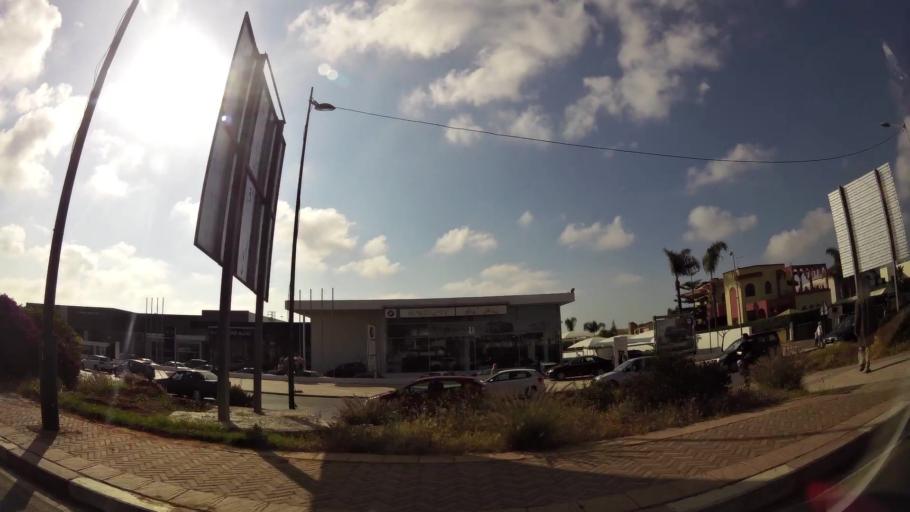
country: MA
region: Rabat-Sale-Zemmour-Zaer
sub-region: Skhirate-Temara
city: Temara
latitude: 33.9481
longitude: -6.8703
